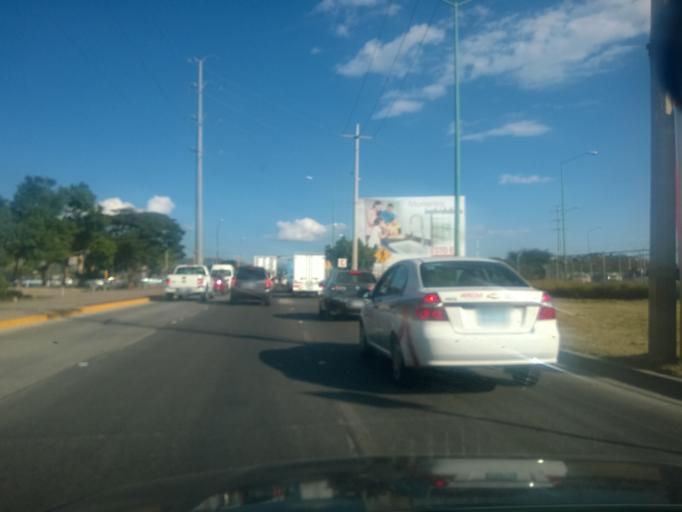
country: MX
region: Guanajuato
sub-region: Leon
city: Medina
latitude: 21.1416
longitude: -101.6338
